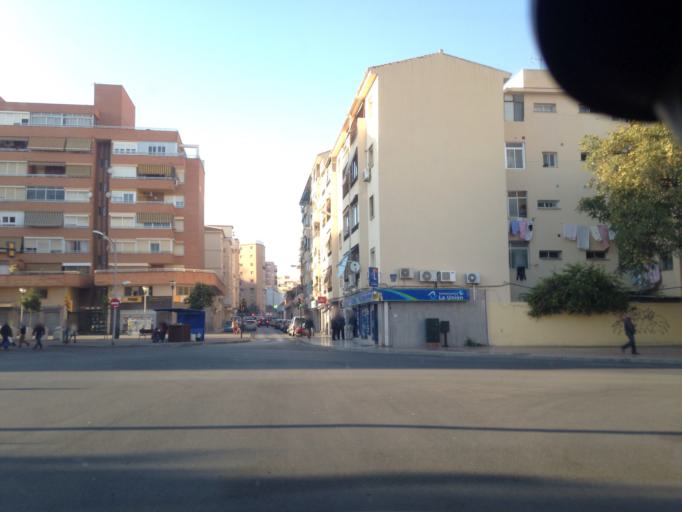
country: ES
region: Andalusia
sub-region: Provincia de Malaga
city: Malaga
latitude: 36.7109
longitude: -4.4384
